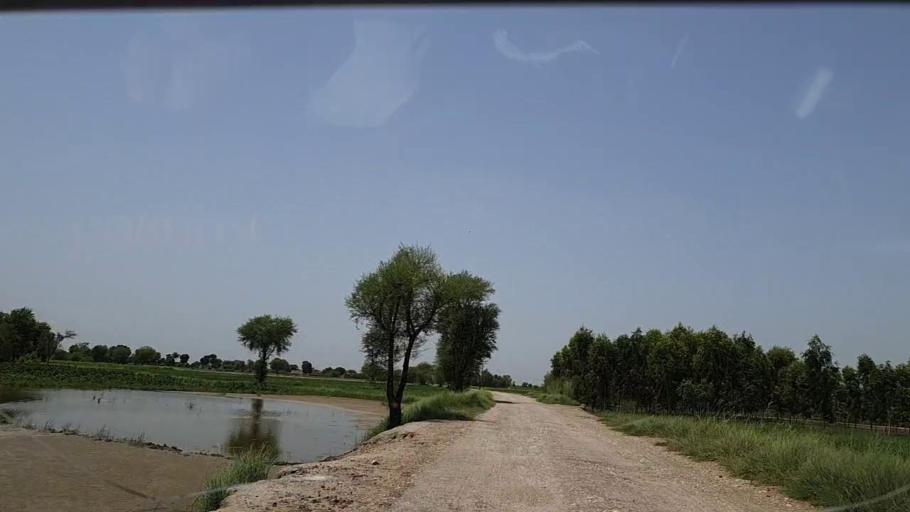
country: PK
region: Sindh
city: Tharu Shah
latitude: 26.9363
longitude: 68.0469
